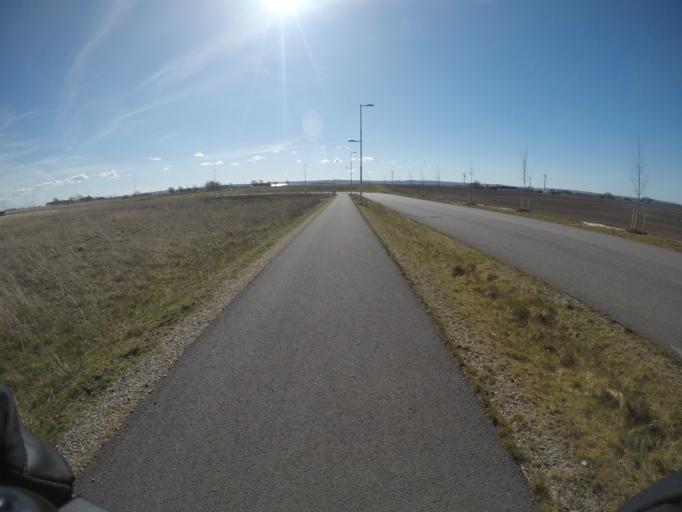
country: SE
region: Halland
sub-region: Laholms Kommun
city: Laholm
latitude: 56.4991
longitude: 13.0031
